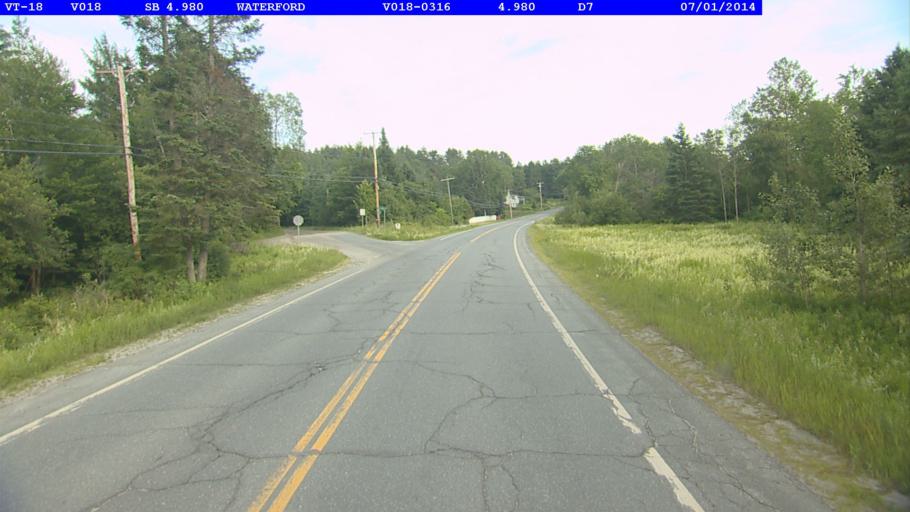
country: US
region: Vermont
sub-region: Caledonia County
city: Saint Johnsbury
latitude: 44.4031
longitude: -71.9237
